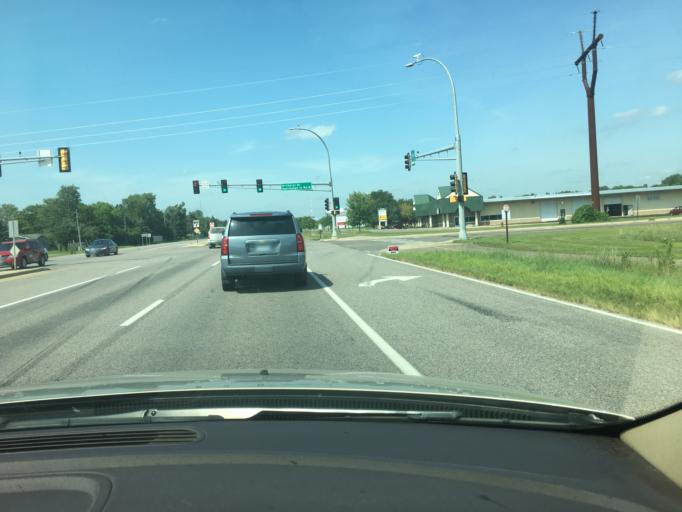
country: US
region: Minnesota
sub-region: Stearns County
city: Saint Cloud
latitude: 45.5217
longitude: -94.1614
